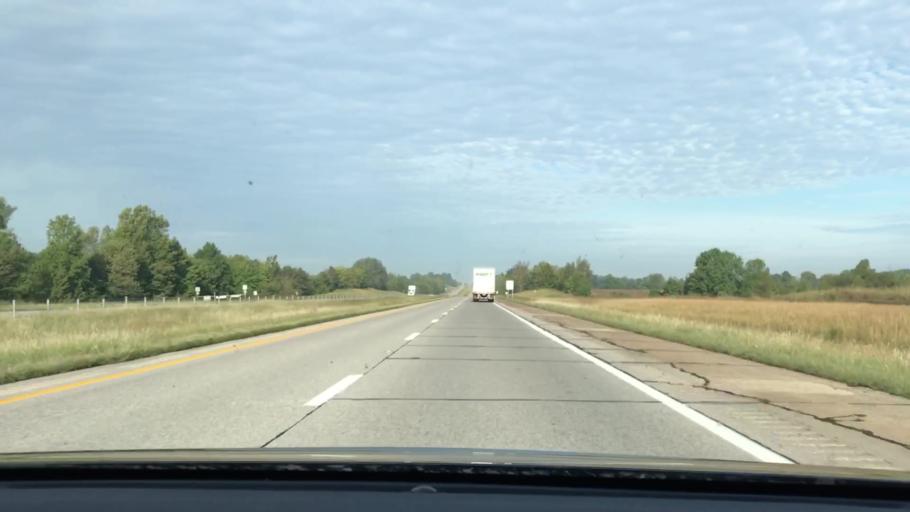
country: US
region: Kentucky
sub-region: Trigg County
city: Cadiz
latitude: 36.9774
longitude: -87.9026
